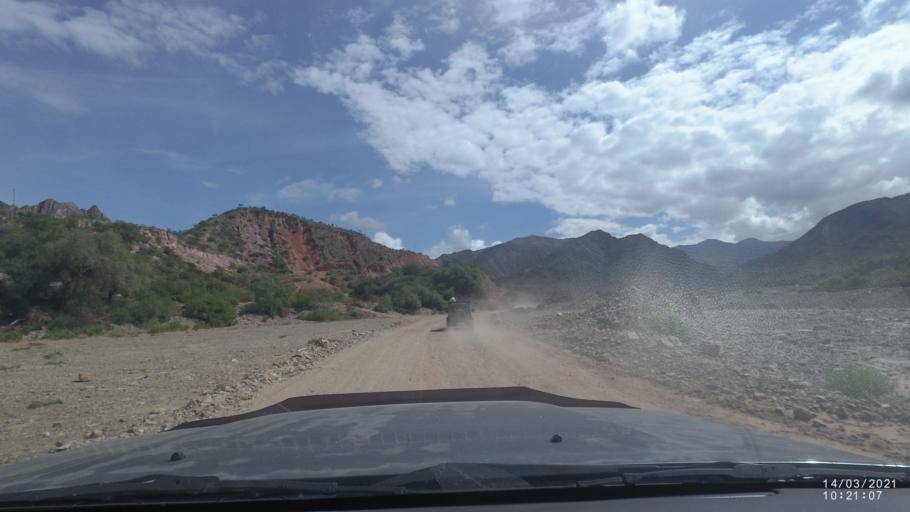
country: BO
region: Cochabamba
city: Cliza
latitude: -17.9265
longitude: -65.8724
